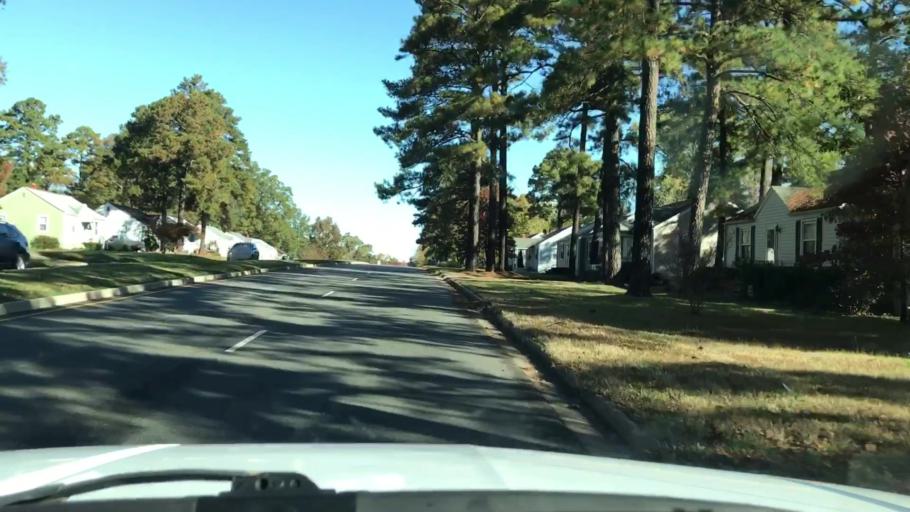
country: US
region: Virginia
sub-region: Henrico County
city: Tuckahoe
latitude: 37.5984
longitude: -77.5292
